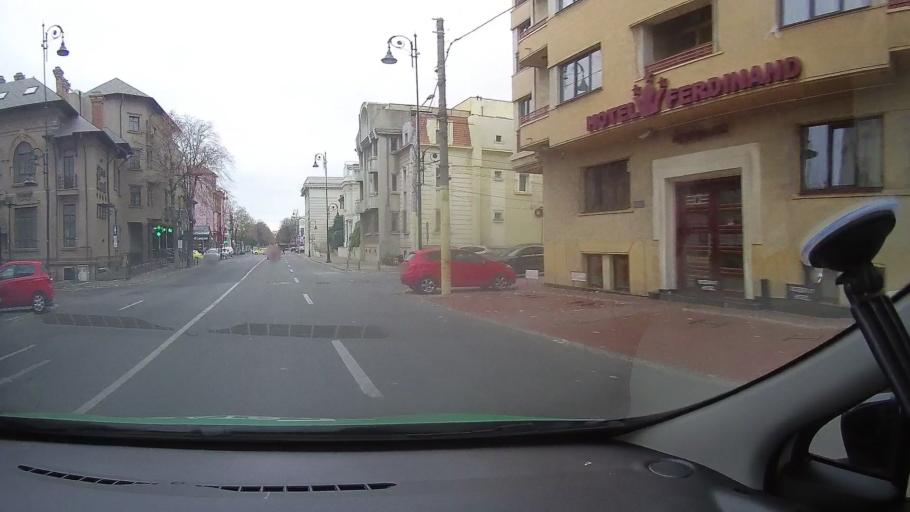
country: RO
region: Constanta
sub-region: Municipiul Constanta
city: Constanta
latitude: 44.1792
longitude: 28.6529
